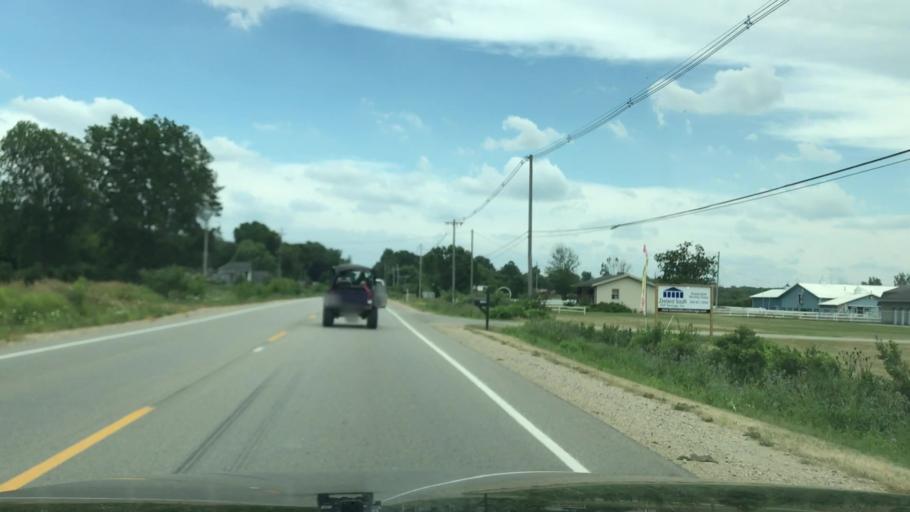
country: US
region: Michigan
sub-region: Ottawa County
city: Zeeland
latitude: 42.7834
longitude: -86.0146
